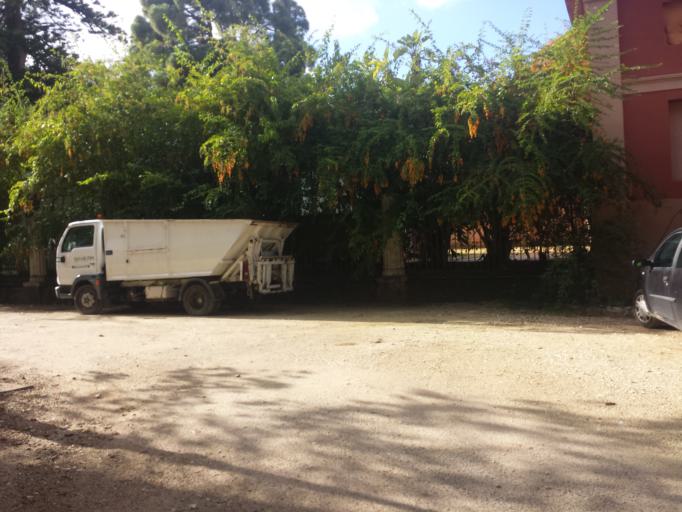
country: IT
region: Sicily
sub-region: Palermo
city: Palermo
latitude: 38.1138
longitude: 13.3739
